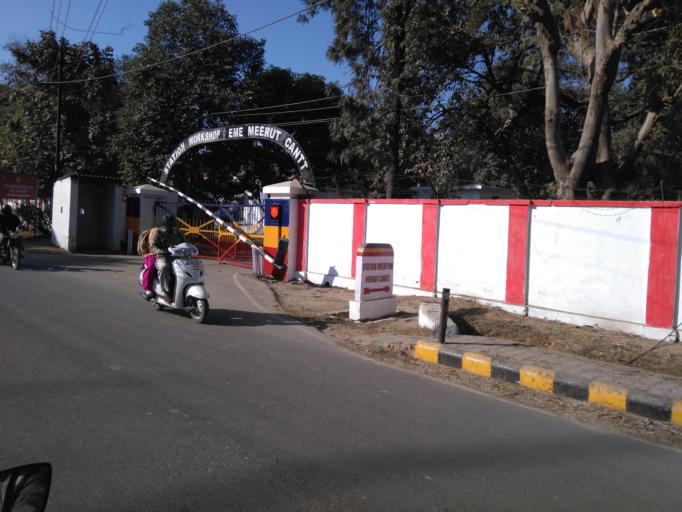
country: IN
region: Uttar Pradesh
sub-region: Meerut
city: Meerut
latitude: 28.9869
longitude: 77.6800
